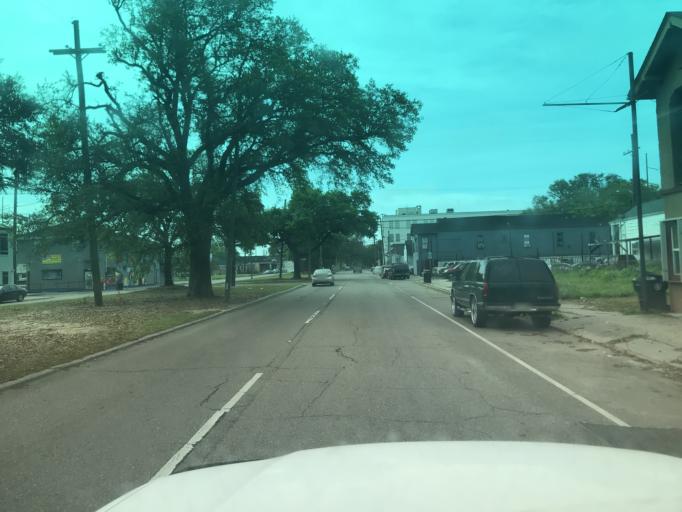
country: US
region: Louisiana
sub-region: Orleans Parish
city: New Orleans
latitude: 29.9778
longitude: -90.0485
